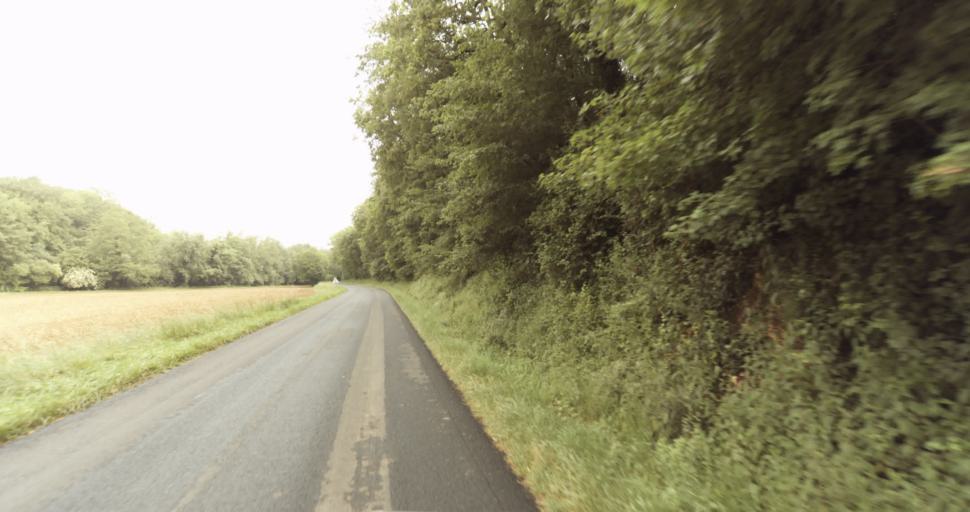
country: FR
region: Aquitaine
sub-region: Departement de la Dordogne
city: Lalinde
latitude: 44.8625
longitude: 0.7748
